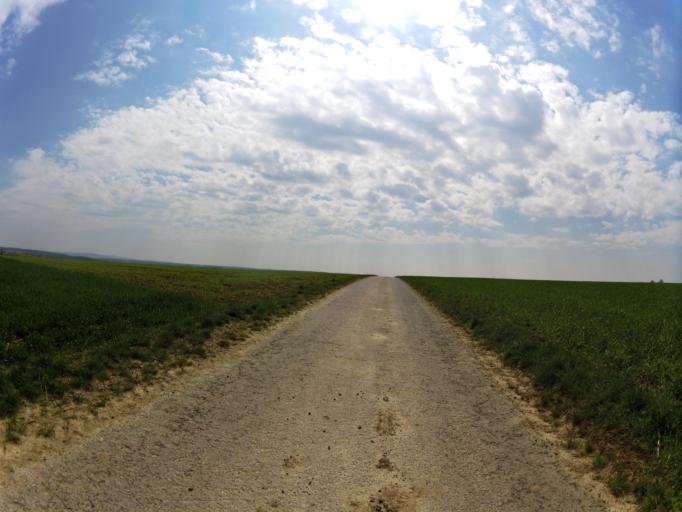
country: DE
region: Bavaria
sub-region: Regierungsbezirk Unterfranken
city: Winterhausen
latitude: 49.6907
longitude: 10.0047
